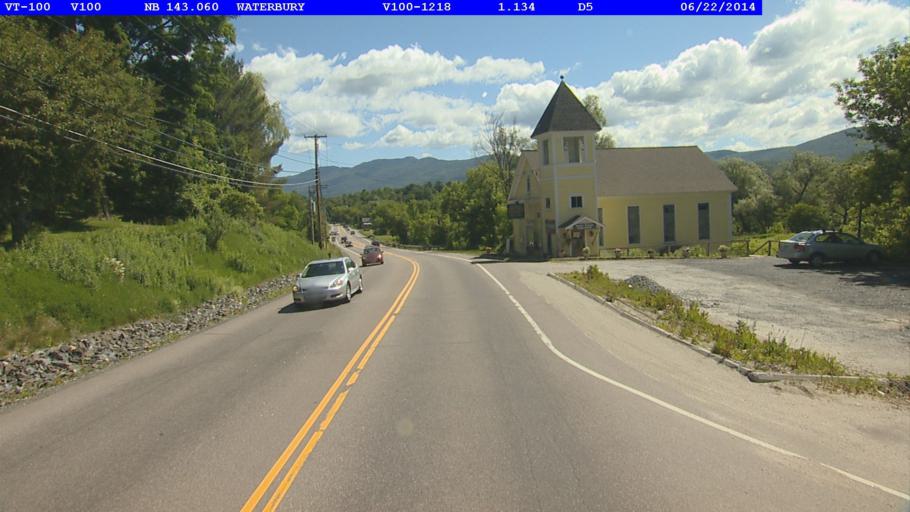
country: US
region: Vermont
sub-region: Washington County
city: Waterbury
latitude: 44.3502
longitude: -72.7421
